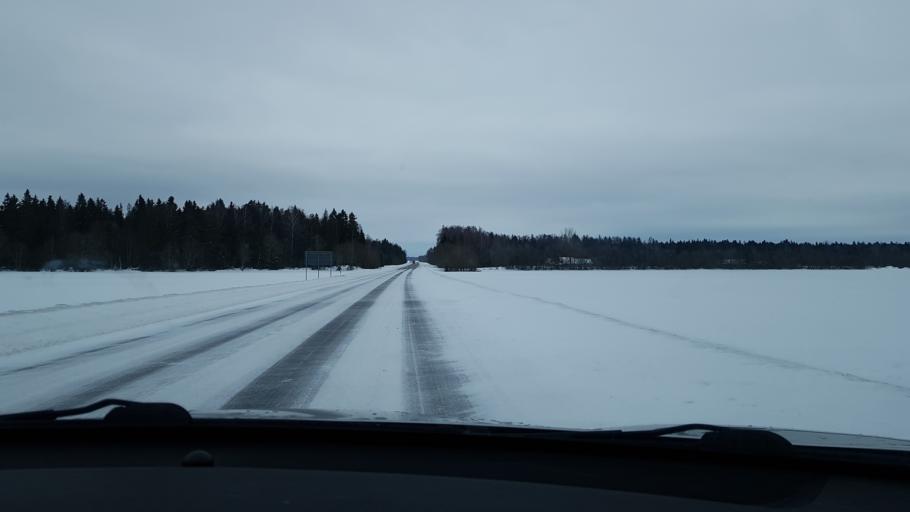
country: EE
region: Jaervamaa
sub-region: Jaerva-Jaani vald
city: Jarva-Jaani
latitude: 59.1375
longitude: 25.7722
